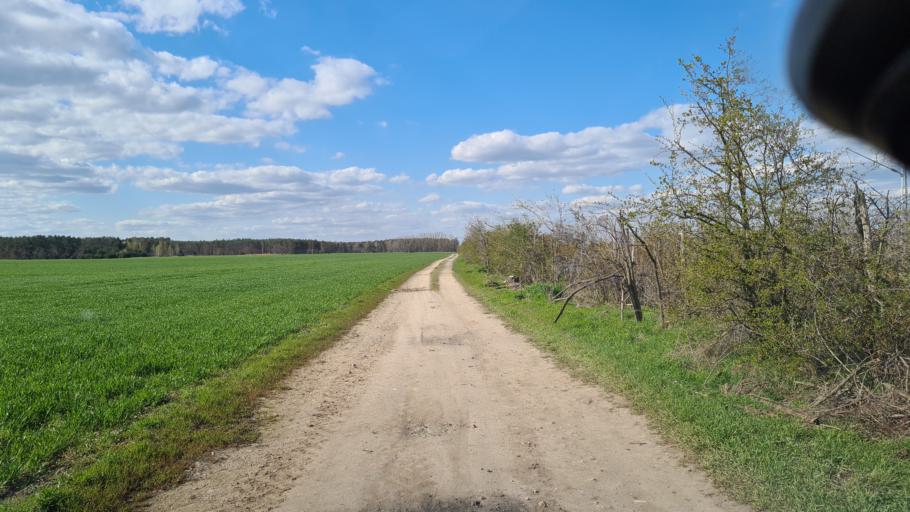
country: DE
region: Brandenburg
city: Falkenberg
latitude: 51.5185
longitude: 13.2733
